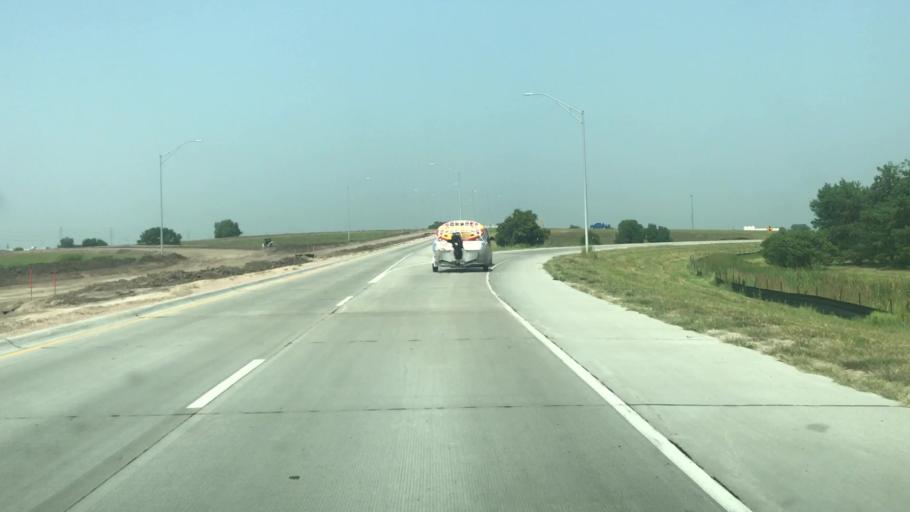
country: US
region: Nebraska
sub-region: Hall County
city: Grand Island
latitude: 40.9496
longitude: -98.3840
